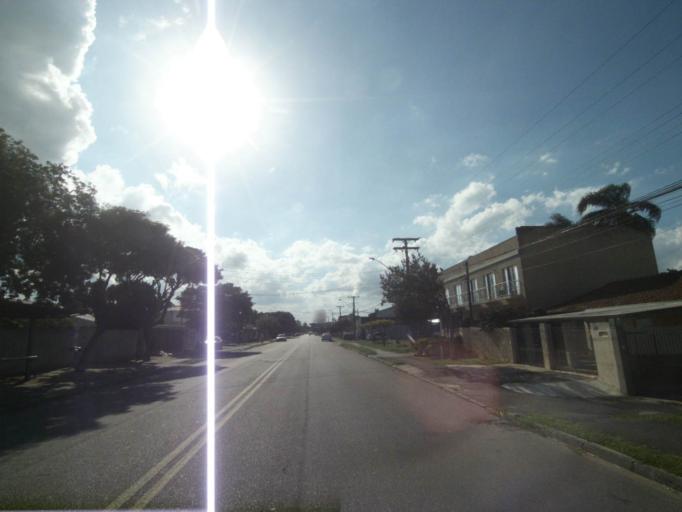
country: BR
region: Parana
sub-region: Pinhais
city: Pinhais
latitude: -25.4376
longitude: -49.2078
